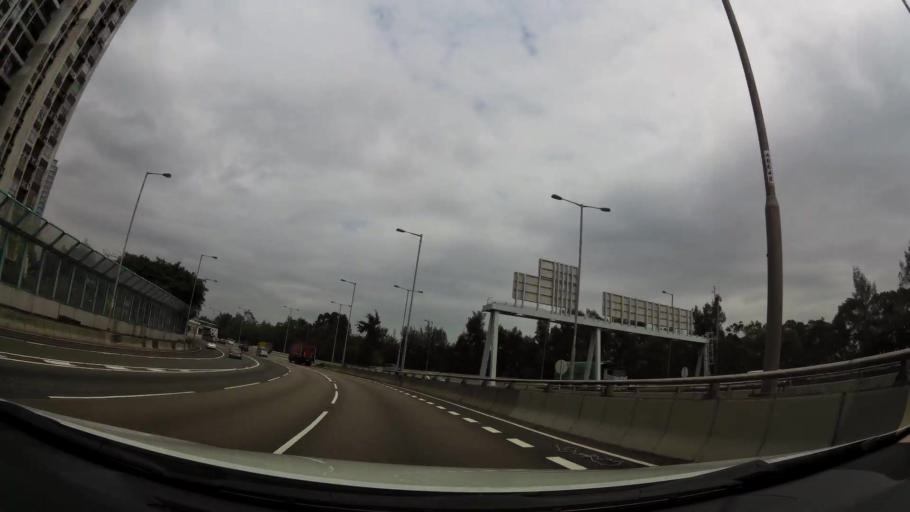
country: HK
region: Kowloon City
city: Kowloon
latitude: 22.2879
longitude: 114.2209
